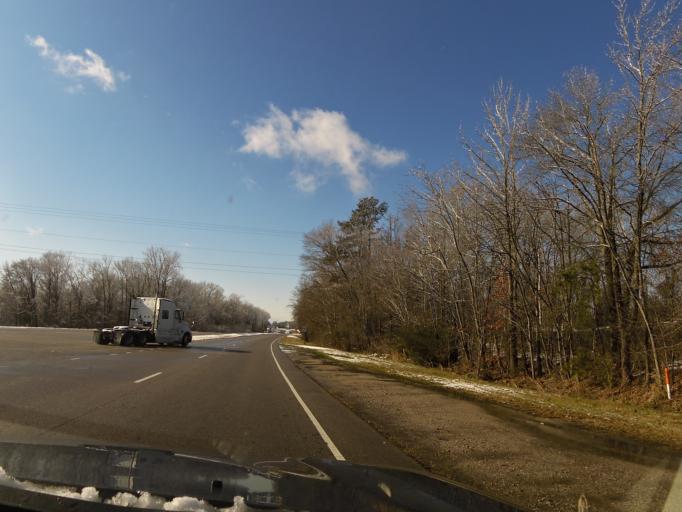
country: US
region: North Carolina
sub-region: Wilson County
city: Wilson
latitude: 35.7329
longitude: -77.8813
